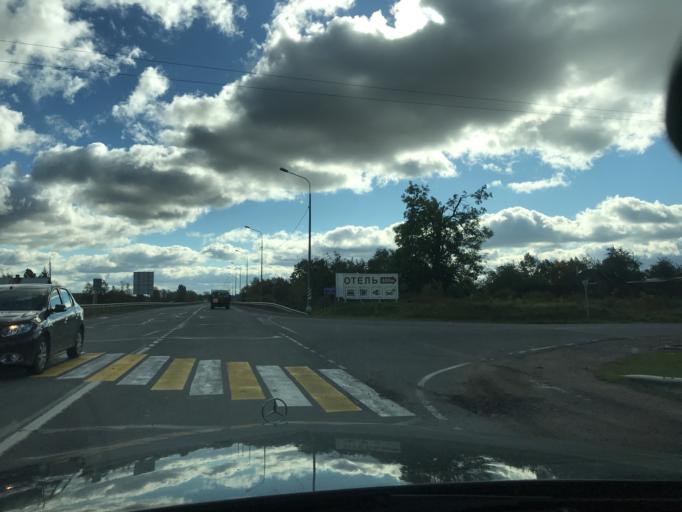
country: RU
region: Pskov
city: Ostrov
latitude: 57.3445
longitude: 28.3704
